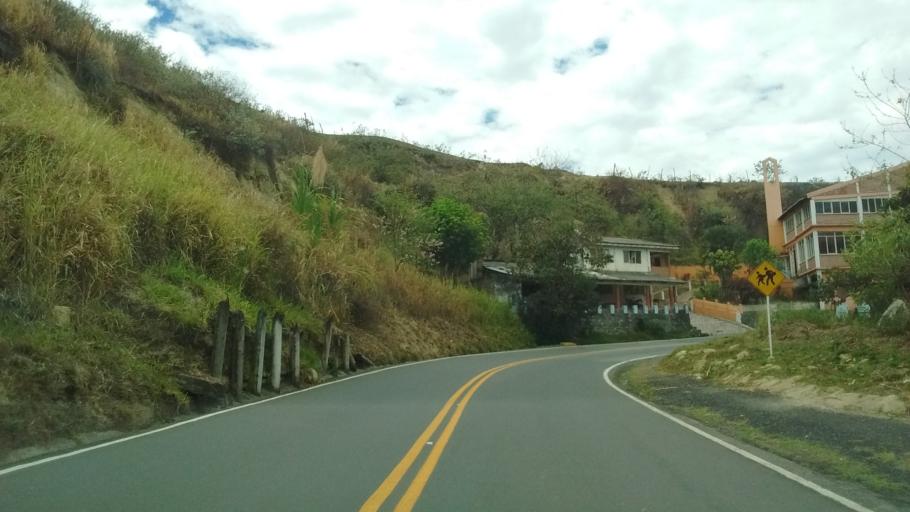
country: CO
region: Cauca
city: La Sierra
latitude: 2.2265
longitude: -76.7963
